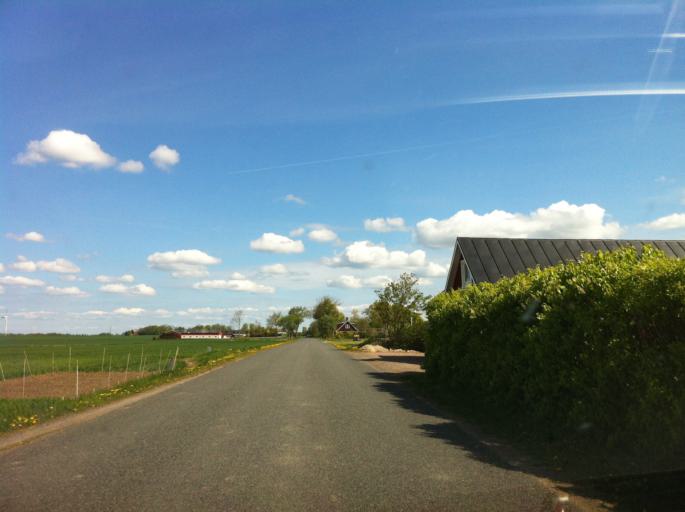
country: SE
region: Skane
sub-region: Landskrona
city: Asmundtorp
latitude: 55.8923
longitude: 12.9950
